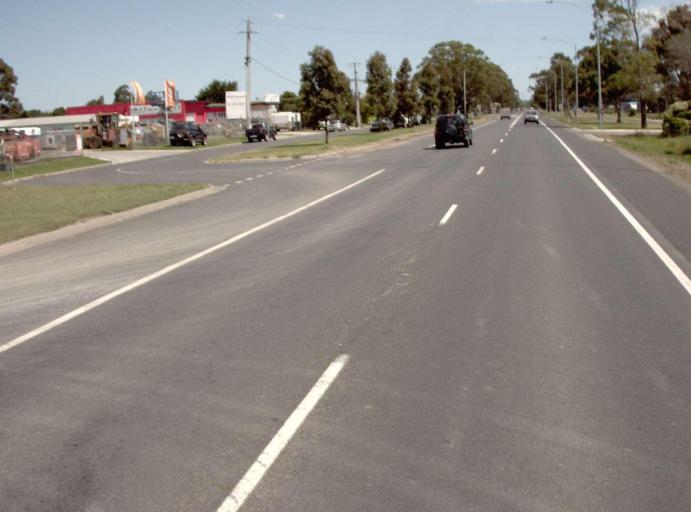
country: AU
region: Victoria
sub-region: Wellington
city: Sale
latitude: -38.0869
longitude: 147.0702
